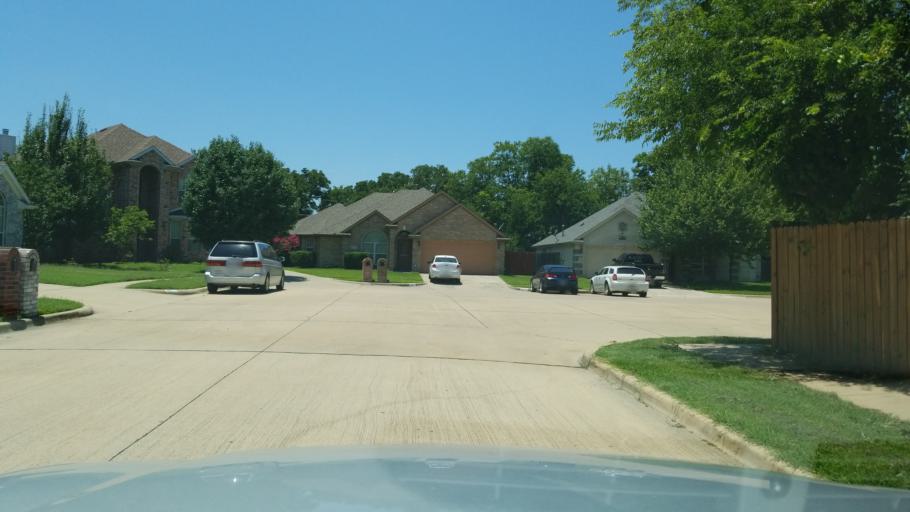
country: US
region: Texas
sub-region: Dallas County
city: Irving
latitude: 32.7994
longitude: -96.9264
